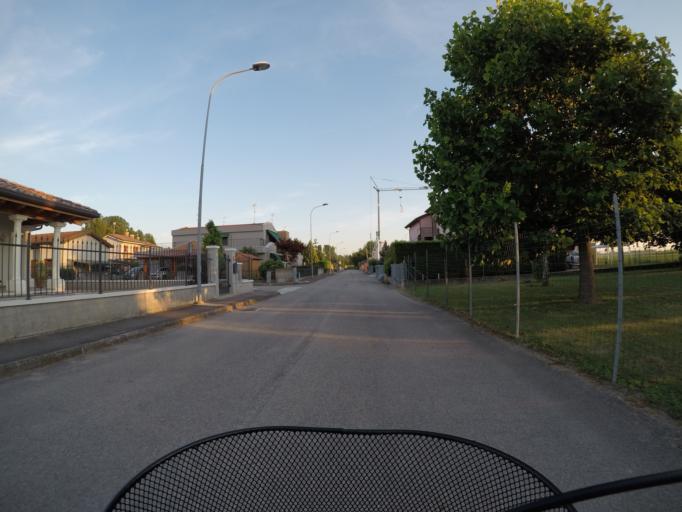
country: IT
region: Veneto
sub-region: Provincia di Rovigo
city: Fratta Polesine
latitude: 45.0343
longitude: 11.6396
